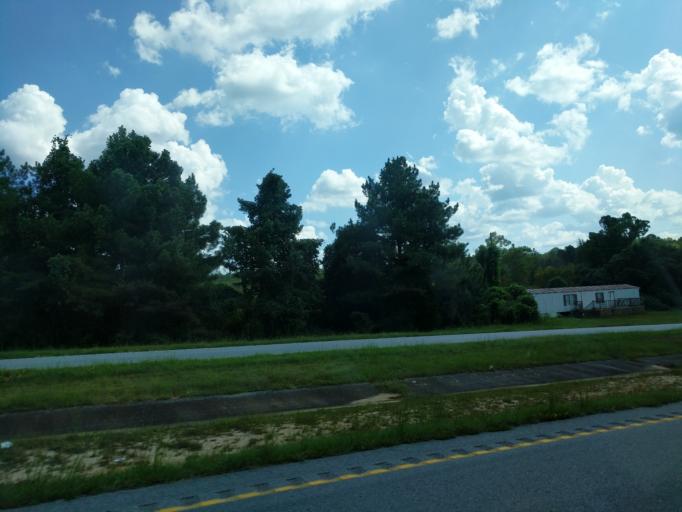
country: US
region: South Carolina
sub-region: Spartanburg County
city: Roebuck
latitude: 34.8205
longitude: -81.9957
